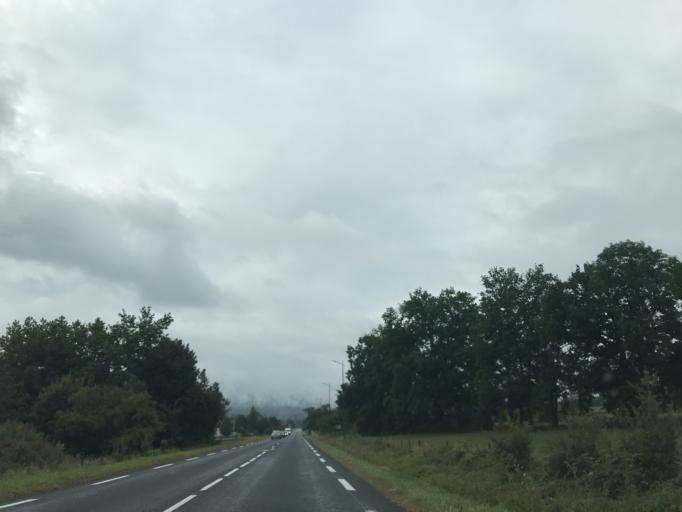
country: FR
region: Auvergne
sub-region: Departement du Puy-de-Dome
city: Arlanc
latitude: 45.3963
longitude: 3.7370
